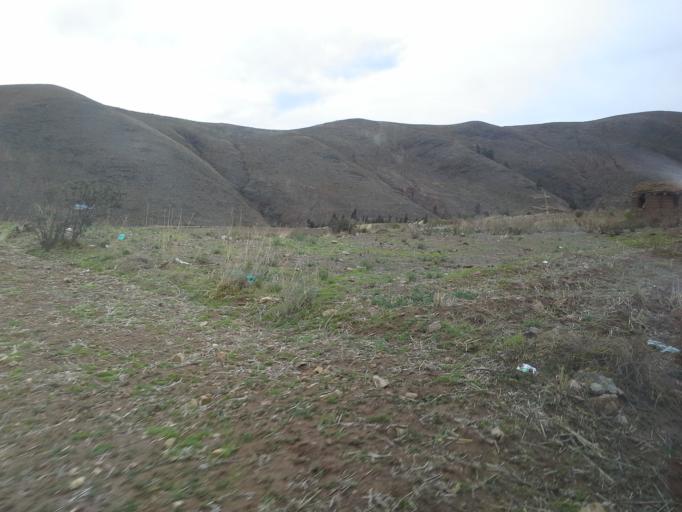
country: BO
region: Cochabamba
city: Colomi
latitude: -17.4098
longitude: -65.8089
